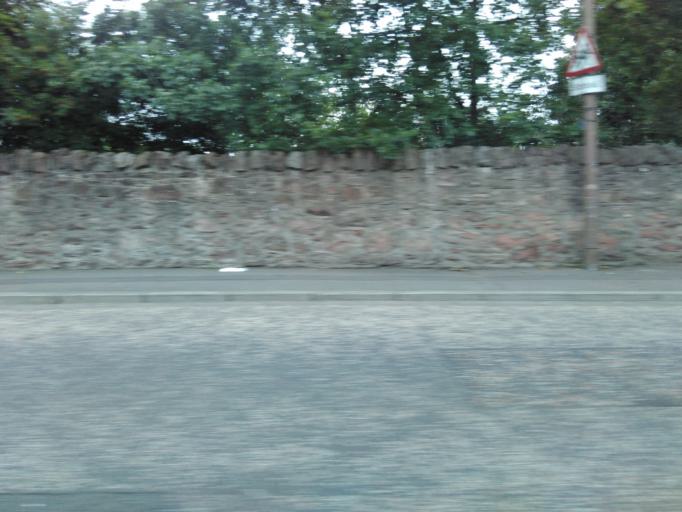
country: GB
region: Scotland
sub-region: Midlothian
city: Loanhead
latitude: 55.9163
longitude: -3.1511
